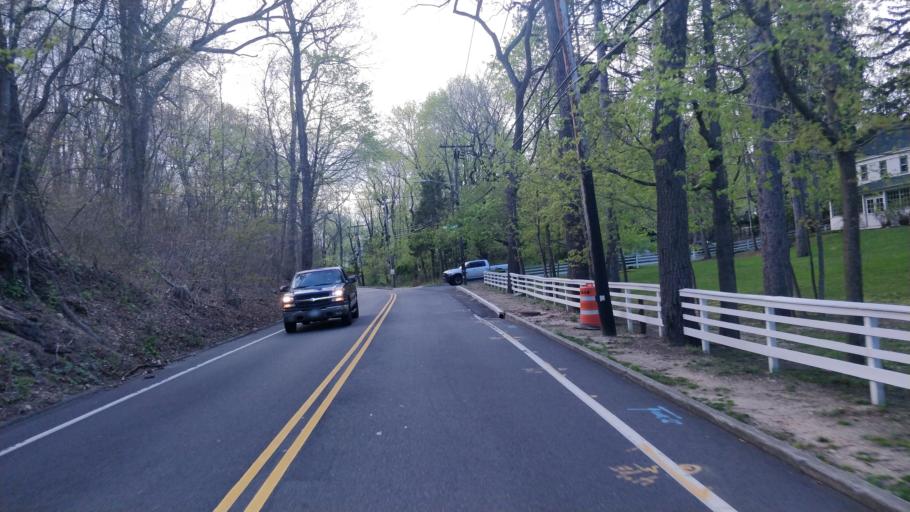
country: US
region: New York
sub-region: Suffolk County
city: Smithtown
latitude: 40.8683
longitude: -73.2040
